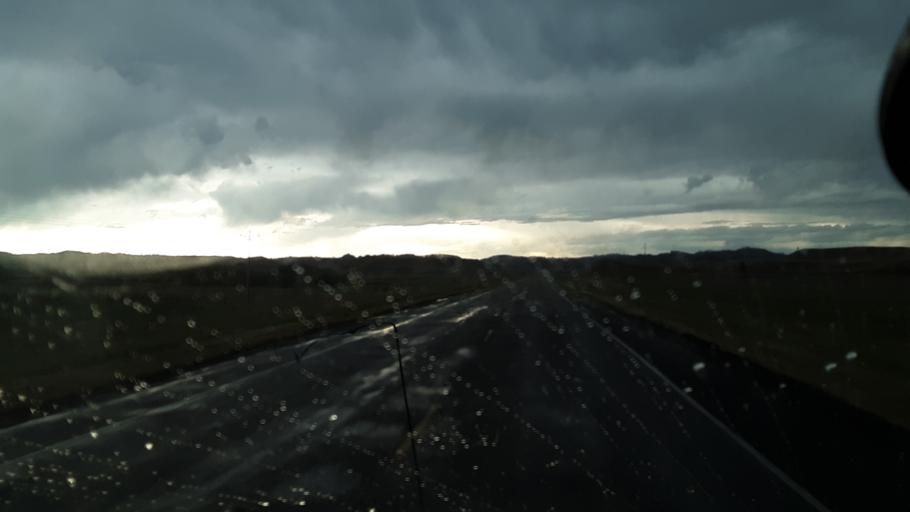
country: US
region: Montana
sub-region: Powder River County
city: Broadus
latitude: 45.5387
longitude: -105.8175
